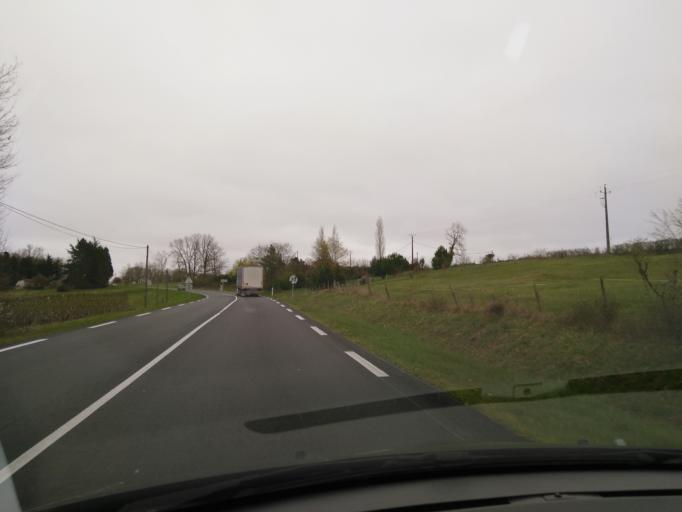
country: FR
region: Aquitaine
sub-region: Departement de la Dordogne
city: Monbazillac
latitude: 44.7384
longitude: 0.5415
